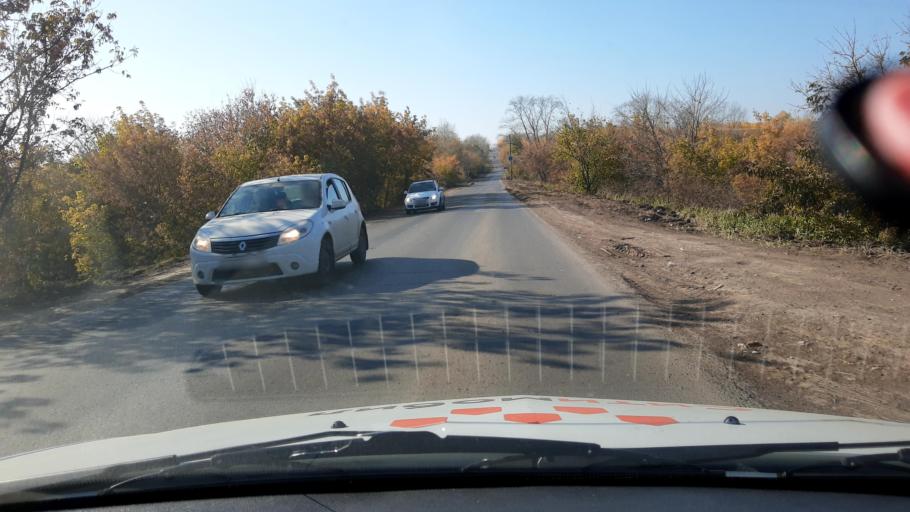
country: RU
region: Bashkortostan
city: Ufa
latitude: 54.8647
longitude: 56.1265
